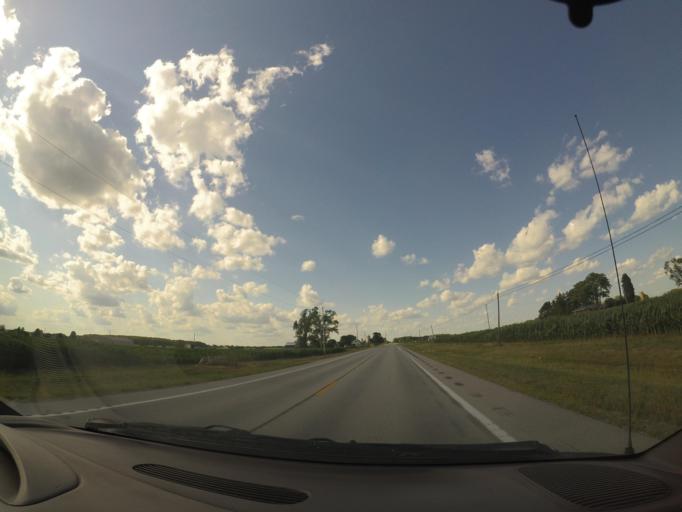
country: US
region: Ohio
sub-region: Wood County
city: Pemberville
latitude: 41.3692
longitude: -83.4167
